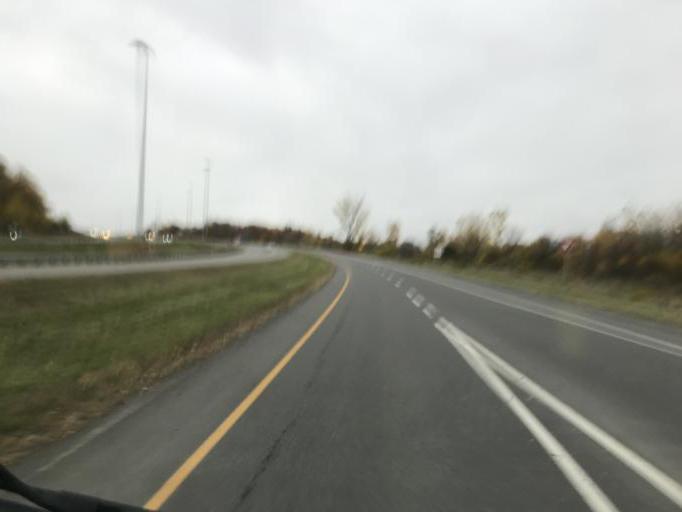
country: CA
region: Quebec
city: Bois-des-Filion
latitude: 45.6735
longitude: -73.7630
